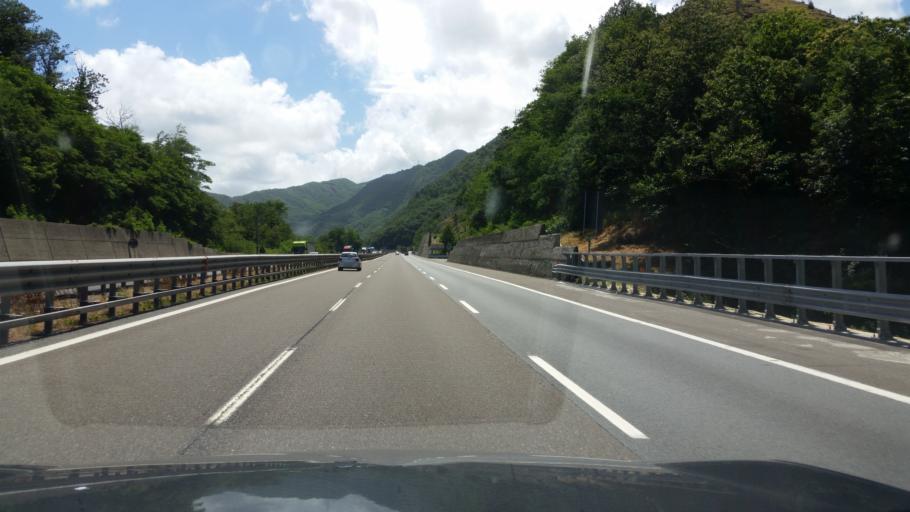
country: IT
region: Liguria
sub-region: Provincia di Genova
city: Rossiglione
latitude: 44.5593
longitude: 8.6678
